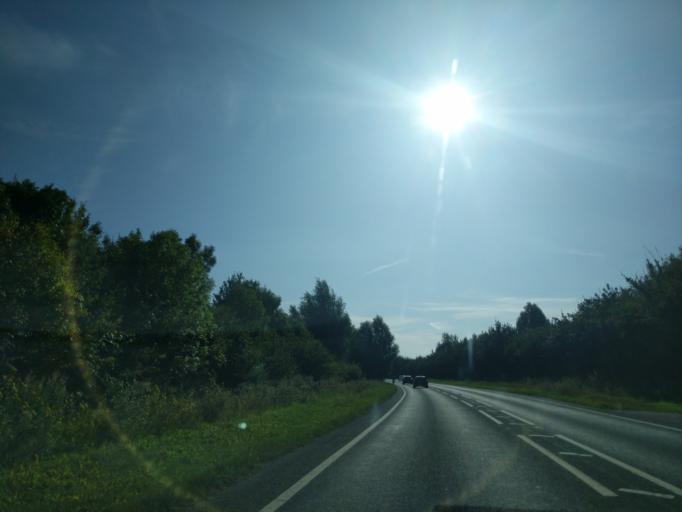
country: GB
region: England
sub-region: Lincolnshire
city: Bourne
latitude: 52.7556
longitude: -0.3759
